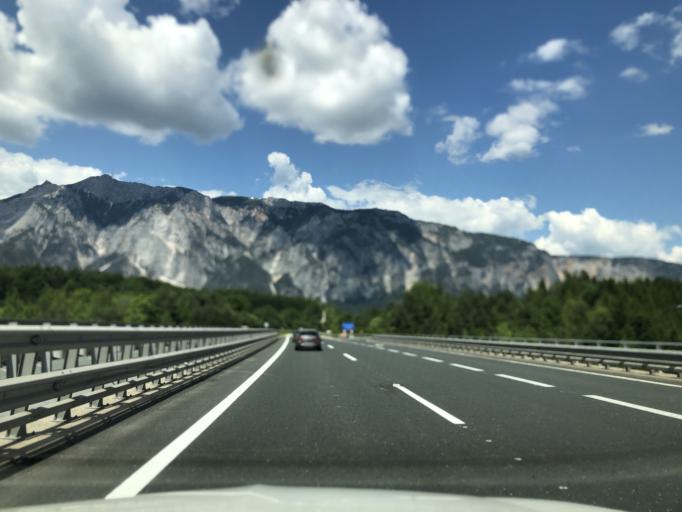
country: AT
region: Carinthia
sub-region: Politischer Bezirk Villach Land
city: Hohenthurn
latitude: 46.5470
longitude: 13.6806
